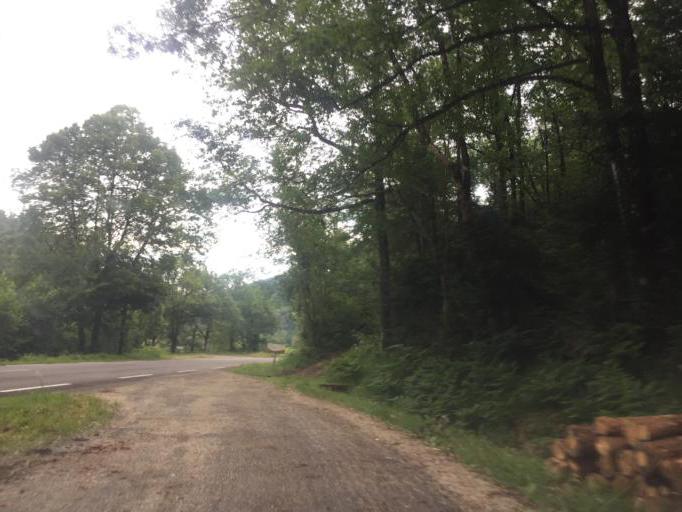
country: FR
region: Rhone-Alpes
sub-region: Departement de l'Ardeche
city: Privas
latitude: 44.7710
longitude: 4.5969
